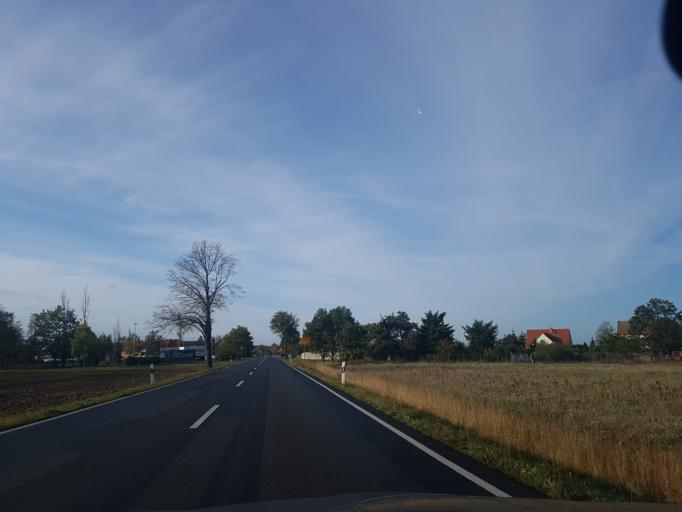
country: DE
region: Saxony
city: Arzberg
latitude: 51.6007
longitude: 13.1278
